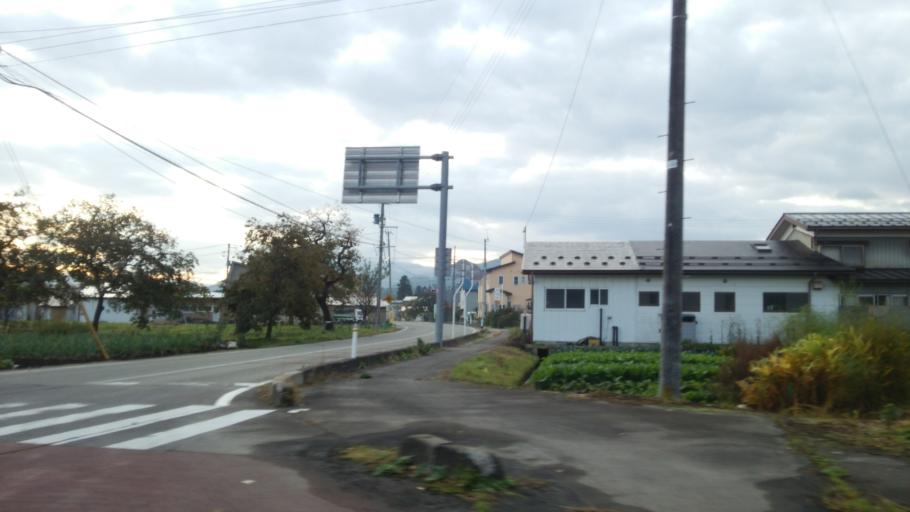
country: JP
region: Fukushima
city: Kitakata
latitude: 37.4445
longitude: 139.8476
